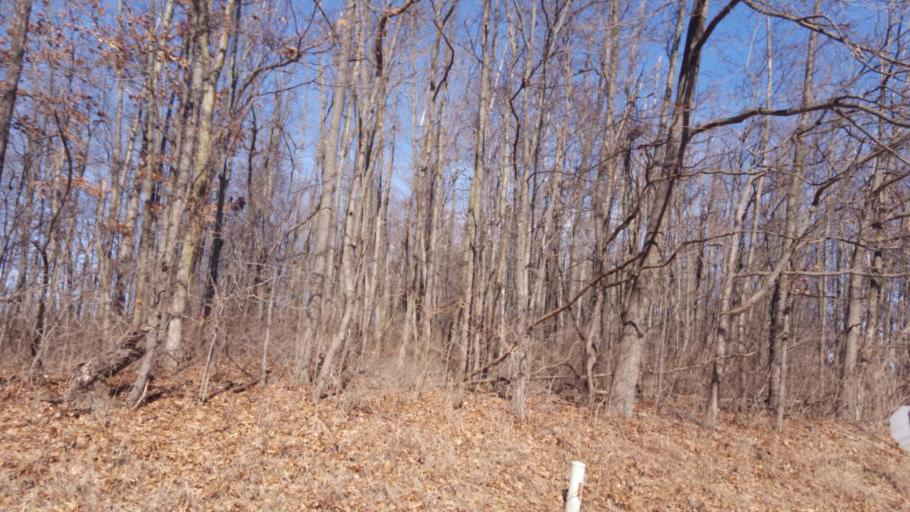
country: US
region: Ohio
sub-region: Knox County
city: Danville
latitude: 40.5347
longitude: -82.3503
